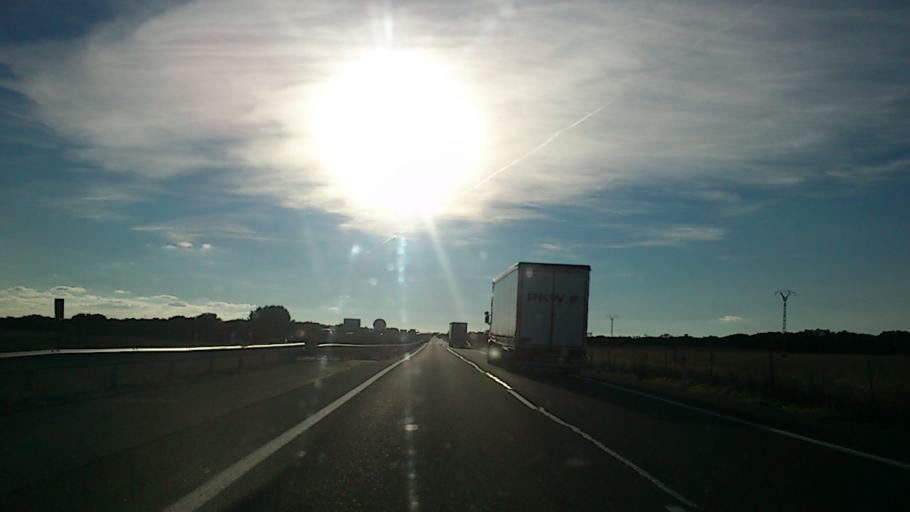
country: ES
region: Castille-La Mancha
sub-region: Provincia de Guadalajara
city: Mirabueno
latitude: 40.9257
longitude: -2.7203
